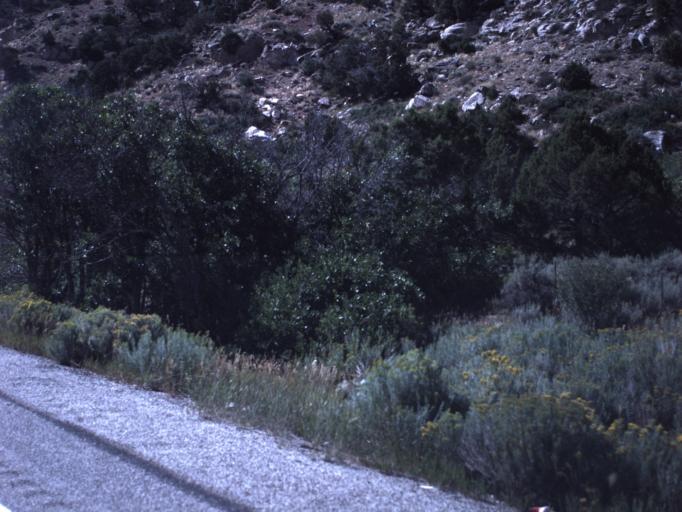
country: US
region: Utah
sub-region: Carbon County
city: Helper
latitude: 40.1967
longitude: -110.9265
